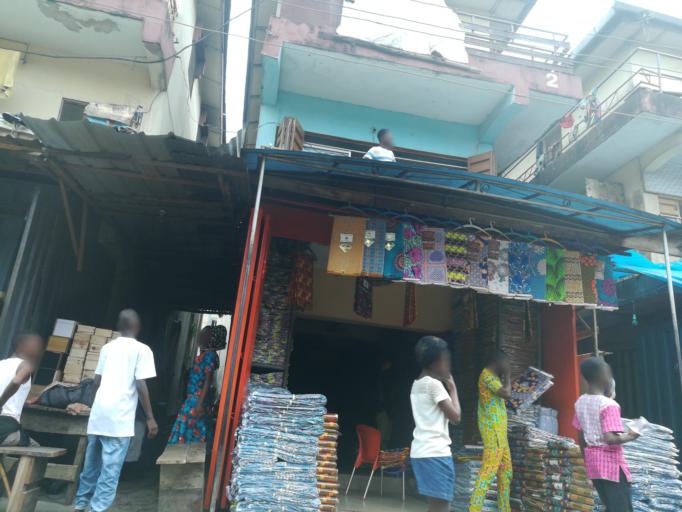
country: NG
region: Lagos
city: Oshodi
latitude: 6.5587
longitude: 3.3498
